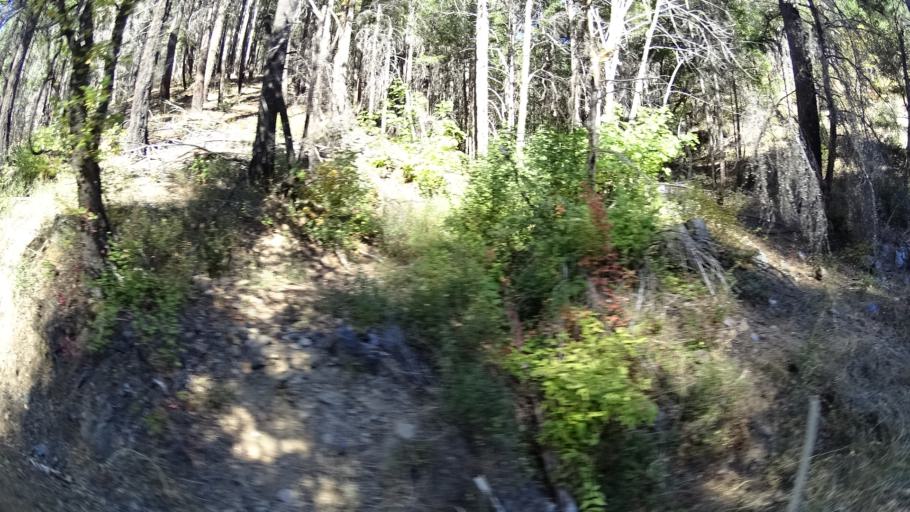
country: US
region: California
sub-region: Siskiyou County
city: Happy Camp
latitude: 41.3204
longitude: -123.1755
